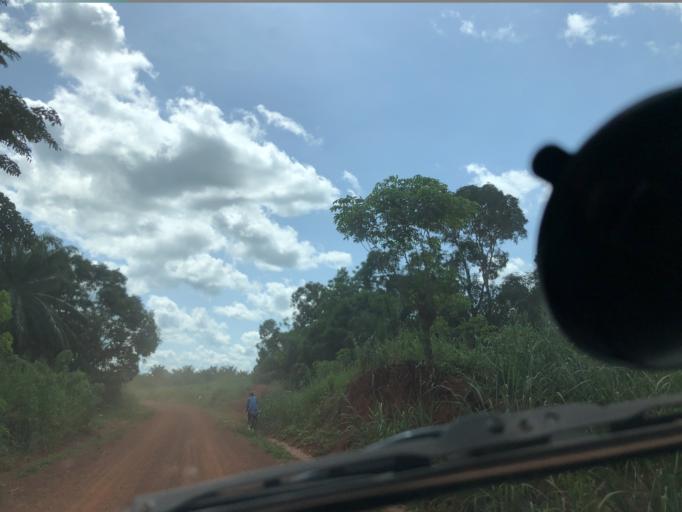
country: CD
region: Equateur
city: Libenge
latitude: 3.7367
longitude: 18.7564
